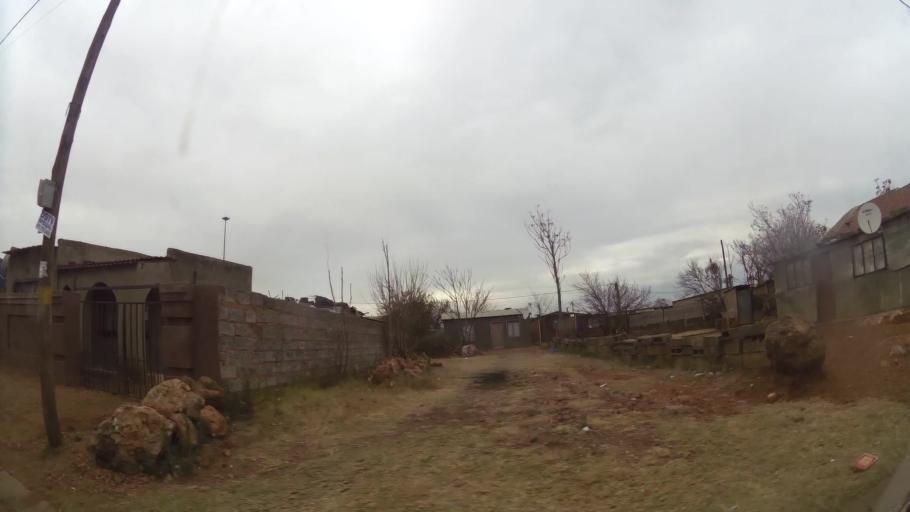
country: ZA
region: Gauteng
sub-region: Ekurhuleni Metropolitan Municipality
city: Germiston
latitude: -26.3857
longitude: 28.1730
